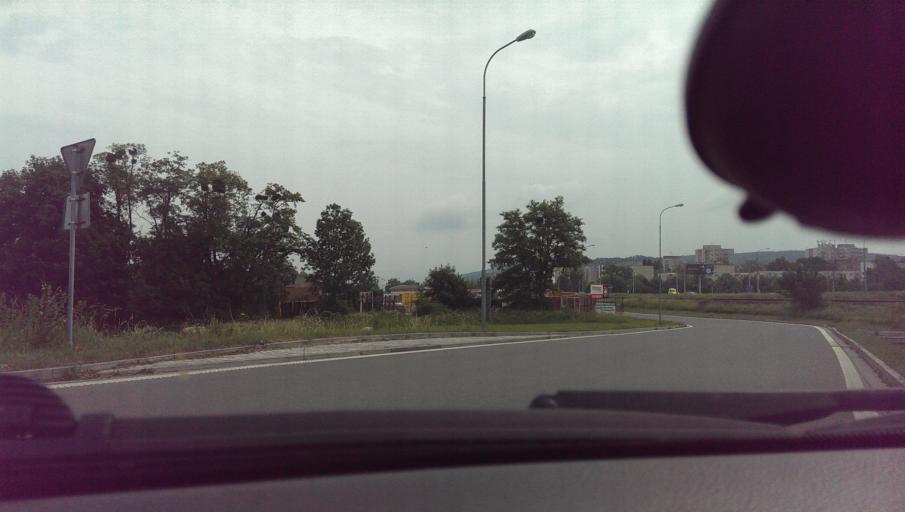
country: CZ
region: Zlin
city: Tecovice
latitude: 49.2063
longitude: 17.5757
